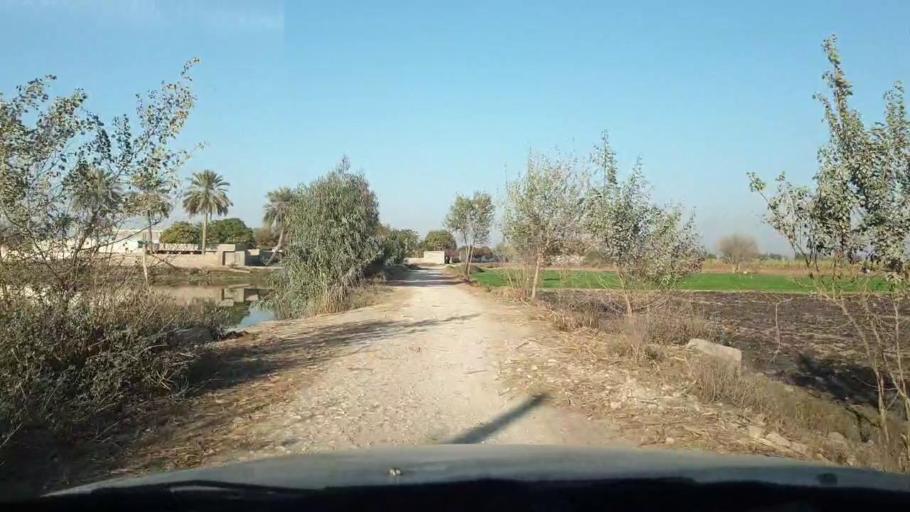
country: PK
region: Sindh
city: Adilpur
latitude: 27.9528
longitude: 69.2308
